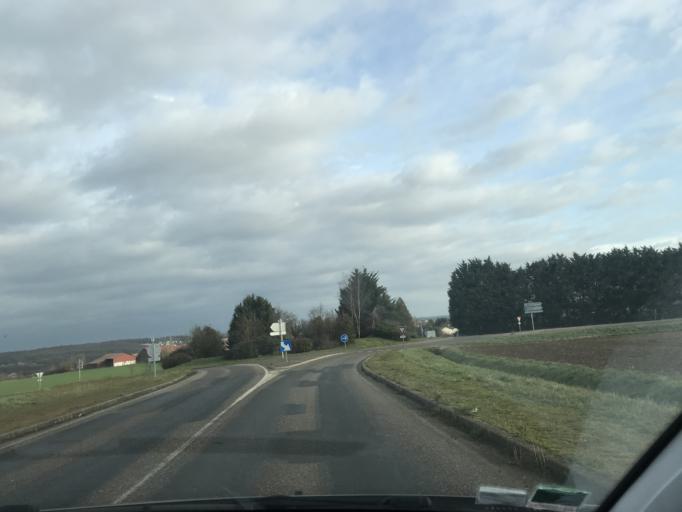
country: FR
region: Lorraine
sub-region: Departement de Meurthe-et-Moselle
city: Auboue
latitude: 49.2005
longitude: 5.9739
